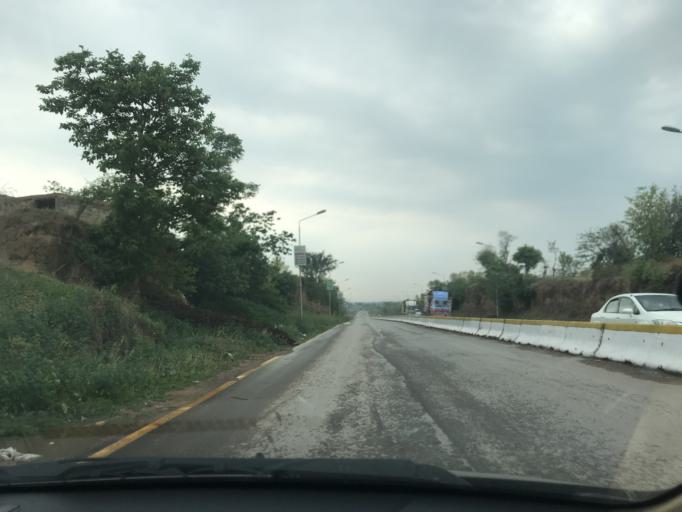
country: PK
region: Islamabad
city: Islamabad
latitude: 33.7002
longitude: 73.1856
